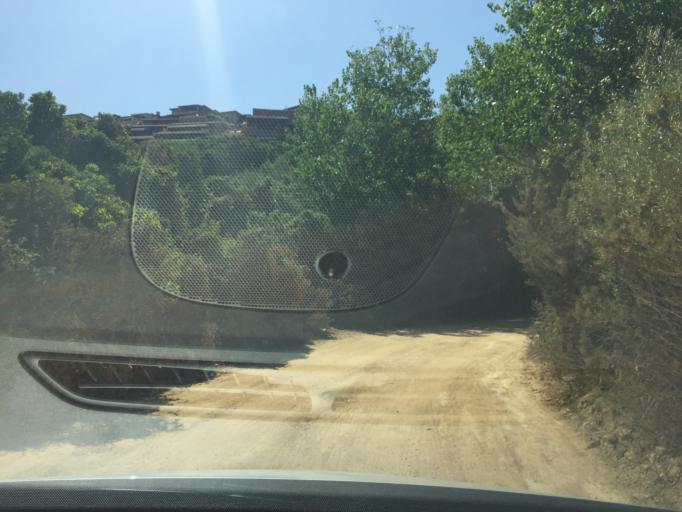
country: IT
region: Sardinia
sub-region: Provincia di Olbia-Tempio
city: San Teodoro
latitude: 40.8396
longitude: 9.7188
